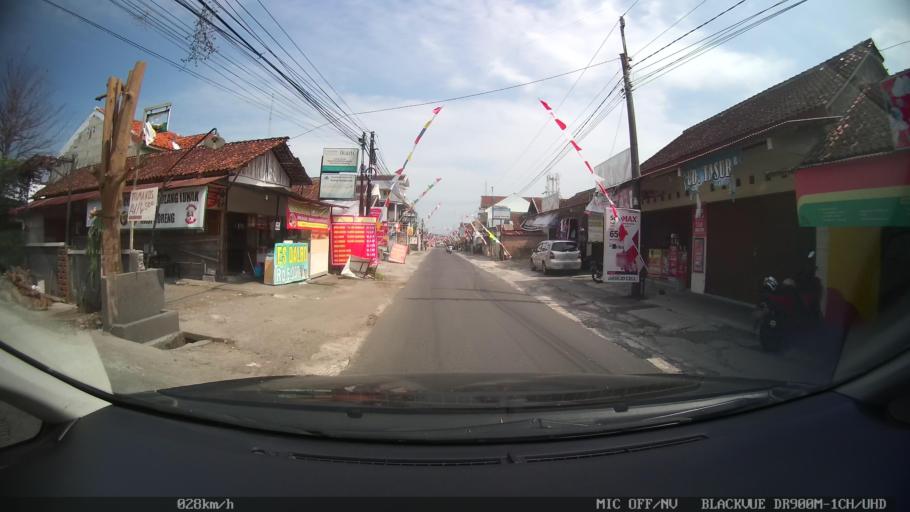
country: ID
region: Daerah Istimewa Yogyakarta
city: Depok
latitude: -7.7611
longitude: 110.4226
